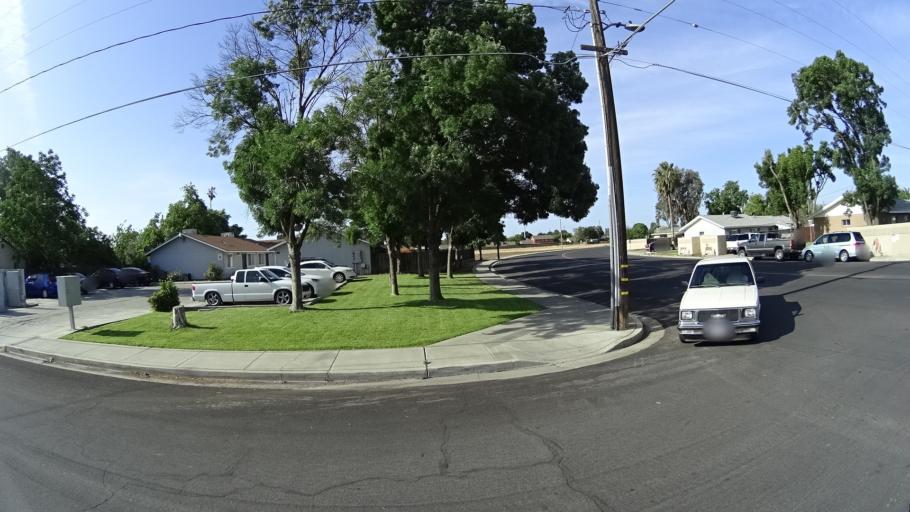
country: US
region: California
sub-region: Kings County
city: Hanford
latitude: 36.3189
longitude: -119.6441
